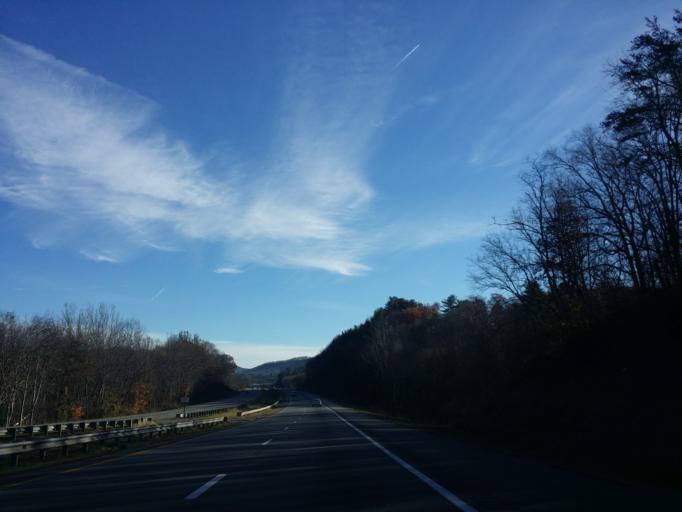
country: US
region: North Carolina
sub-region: Buncombe County
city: Black Mountain
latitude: 35.6020
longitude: -82.3557
